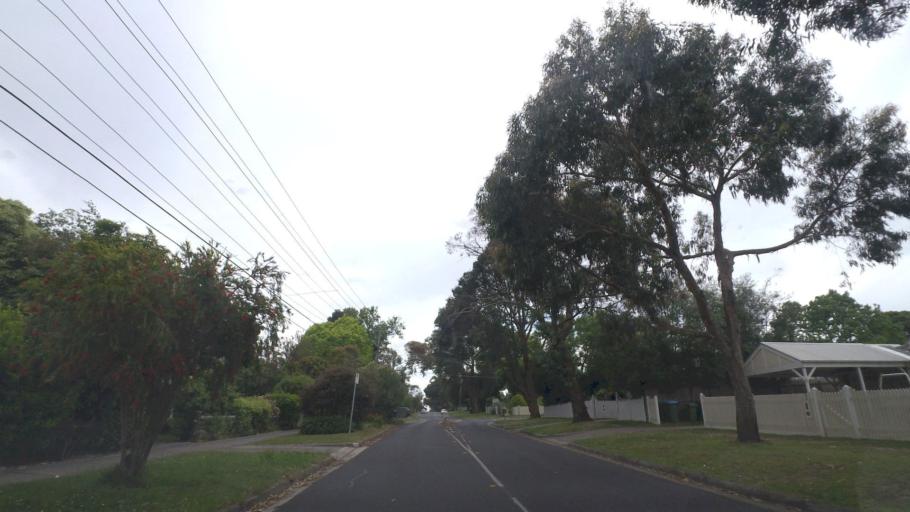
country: AU
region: Victoria
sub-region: Maroondah
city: Croydon North
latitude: -37.7993
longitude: 145.3004
